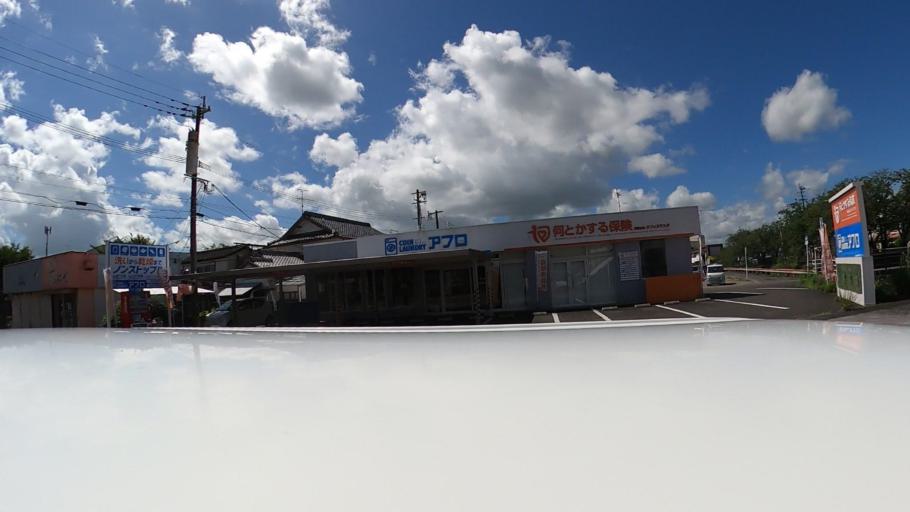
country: JP
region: Miyazaki
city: Tsuma
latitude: 32.1096
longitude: 131.4045
